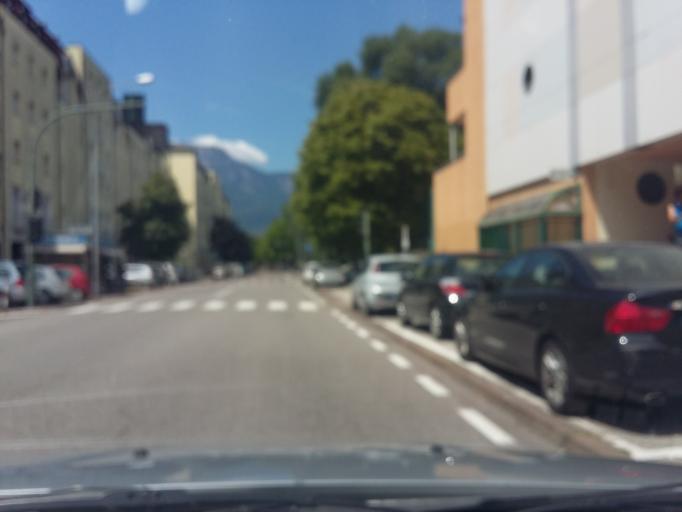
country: IT
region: Trentino-Alto Adige
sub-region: Bolzano
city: Bolzano
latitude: 46.4886
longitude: 11.3274
